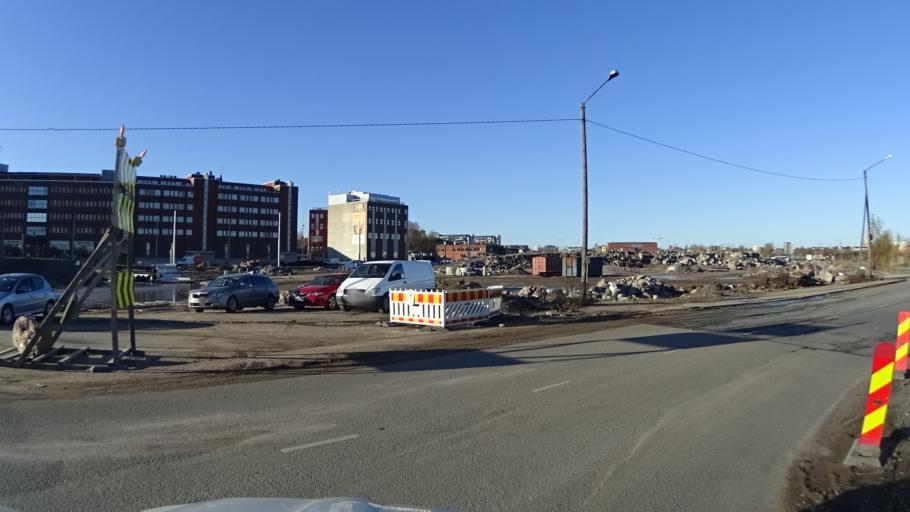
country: FI
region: Uusimaa
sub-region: Helsinki
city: Helsinki
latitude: 60.1908
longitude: 24.9814
